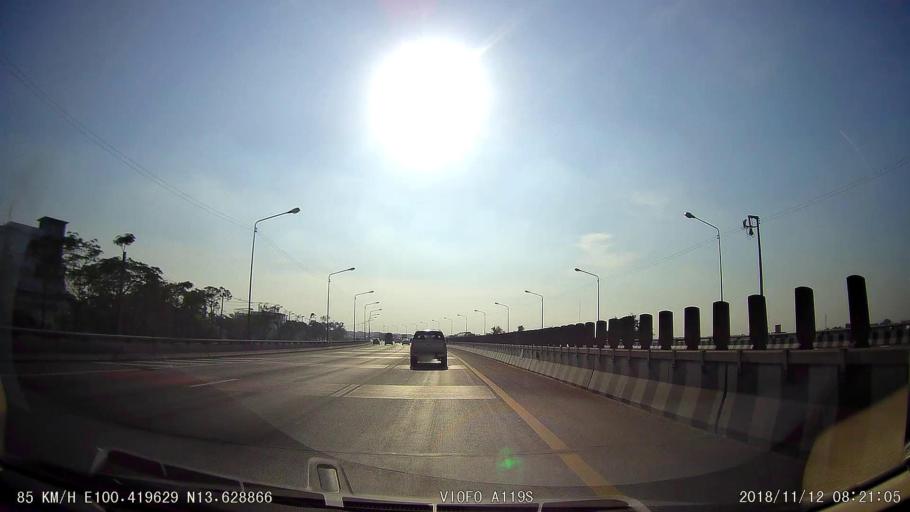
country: TH
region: Bangkok
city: Bang Khun Thian
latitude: 13.6287
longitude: 100.4199
